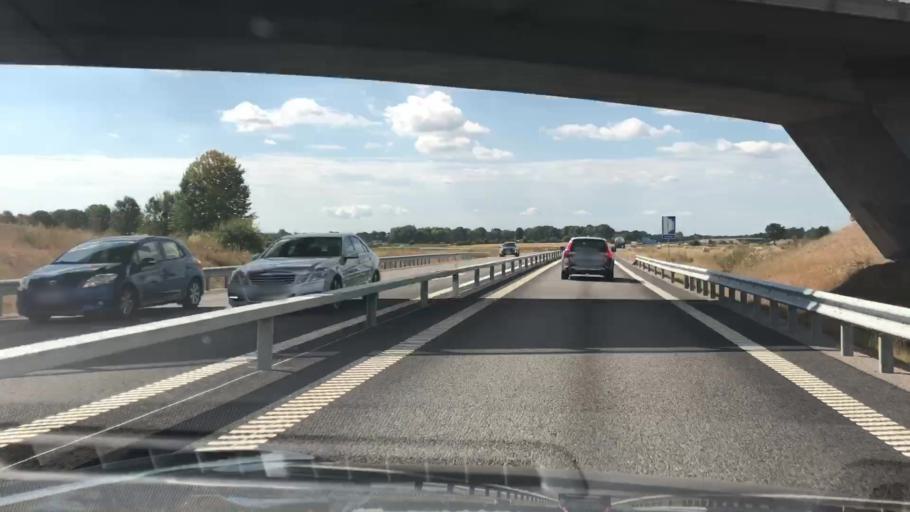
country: SE
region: Kalmar
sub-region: Kalmar Kommun
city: Rinkabyholm
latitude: 56.6487
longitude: 16.2377
